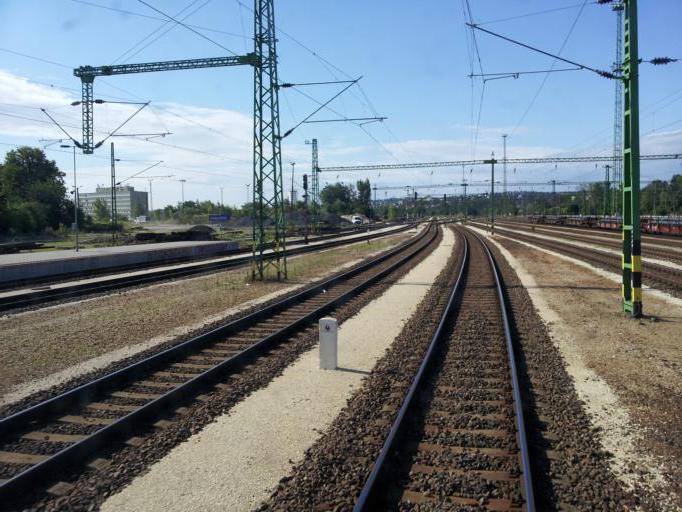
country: HU
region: Budapest
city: Budapest XI. keruelet
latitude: 47.4623
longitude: 19.0206
